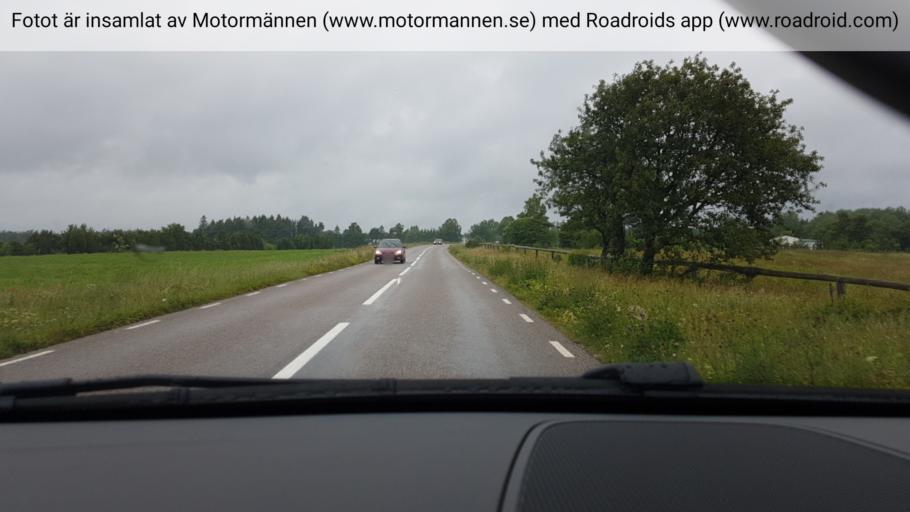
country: SE
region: Gotland
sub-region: Gotland
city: Slite
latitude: 57.6487
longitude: 18.7691
